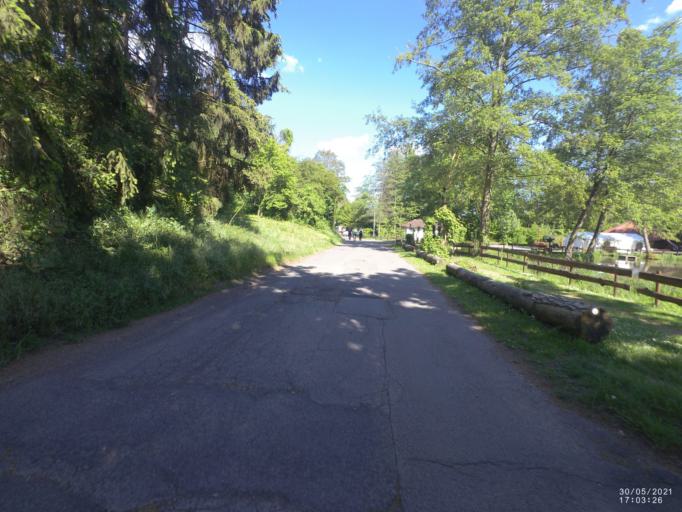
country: DE
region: Rheinland-Pfalz
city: Rhens
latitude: 50.2820
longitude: 7.6050
